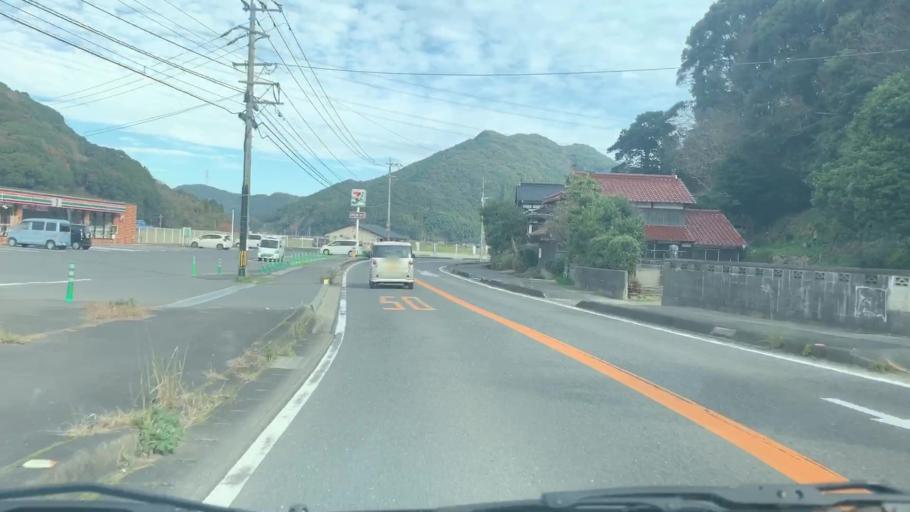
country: JP
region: Saga Prefecture
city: Karatsu
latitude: 33.3556
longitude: 130.0053
